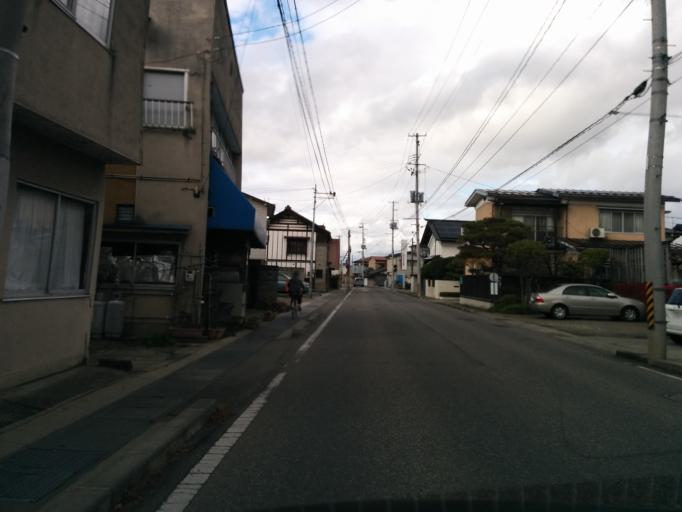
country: JP
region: Fukushima
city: Kitakata
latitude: 37.4868
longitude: 139.9117
